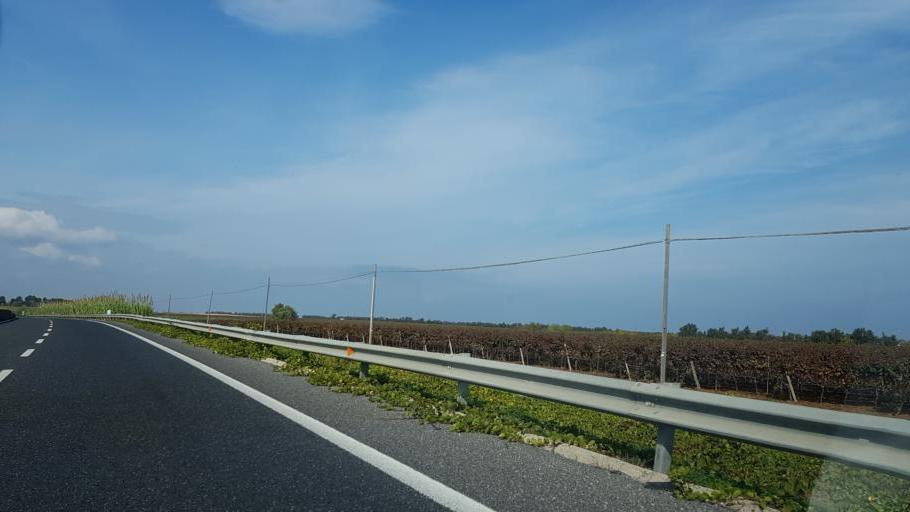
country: IT
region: Apulia
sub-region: Provincia di Brindisi
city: Brindisi
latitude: 40.6666
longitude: 17.8731
